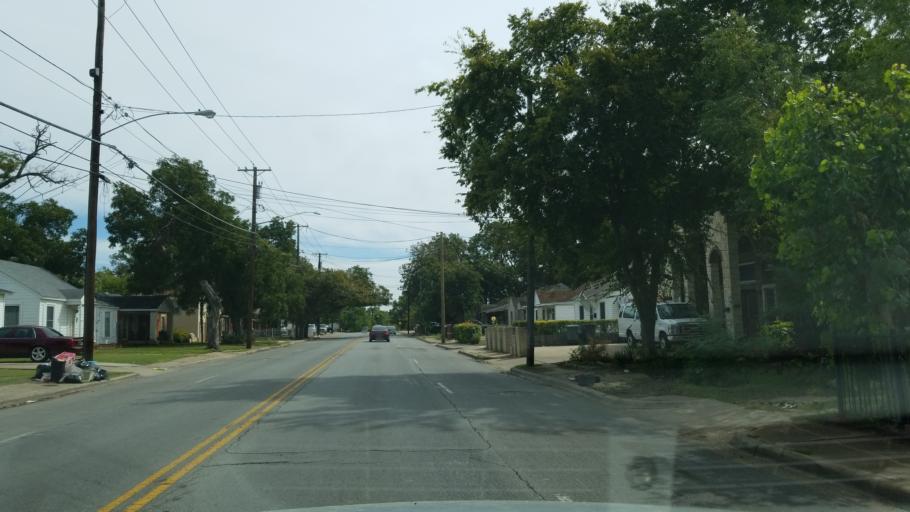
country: US
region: Texas
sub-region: Dallas County
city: Dallas
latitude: 32.7821
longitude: -96.7201
